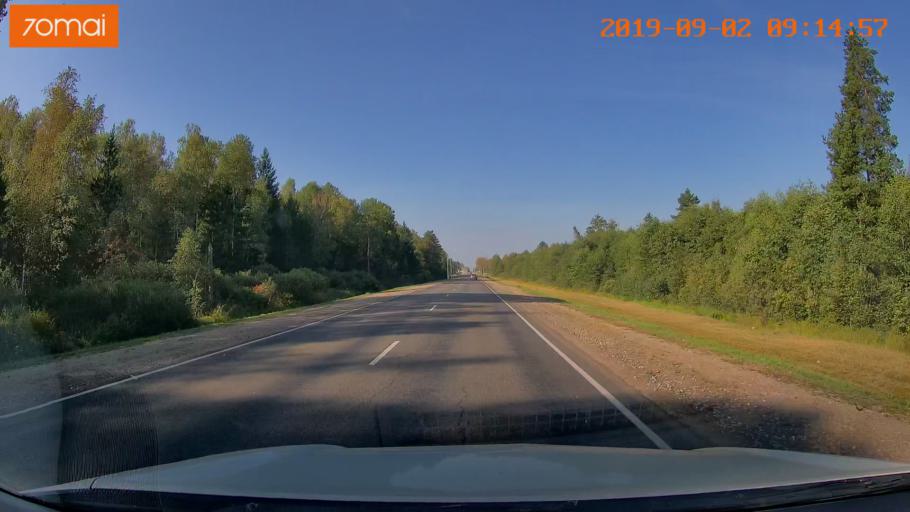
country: RU
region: Kaluga
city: Nikola-Lenivets
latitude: 54.8422
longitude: 35.5031
